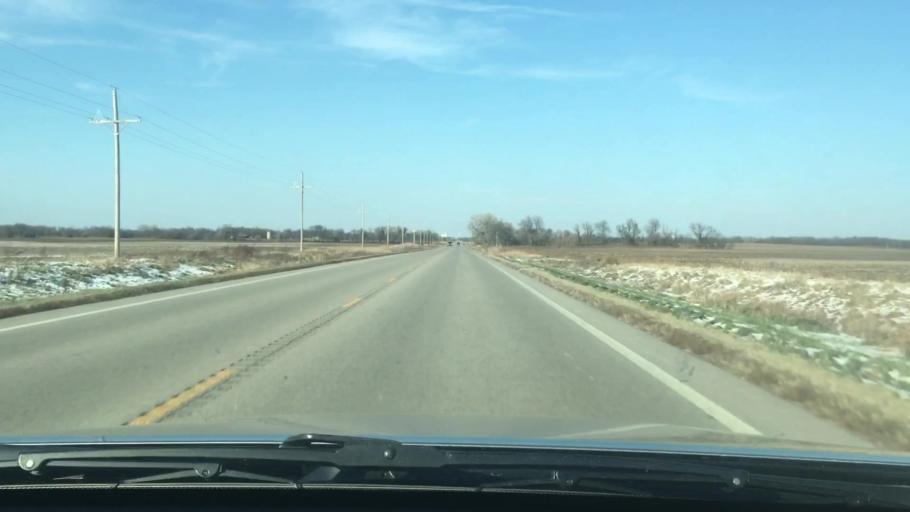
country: US
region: Kansas
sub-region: Rice County
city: Lyons
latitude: 38.2932
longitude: -98.2018
